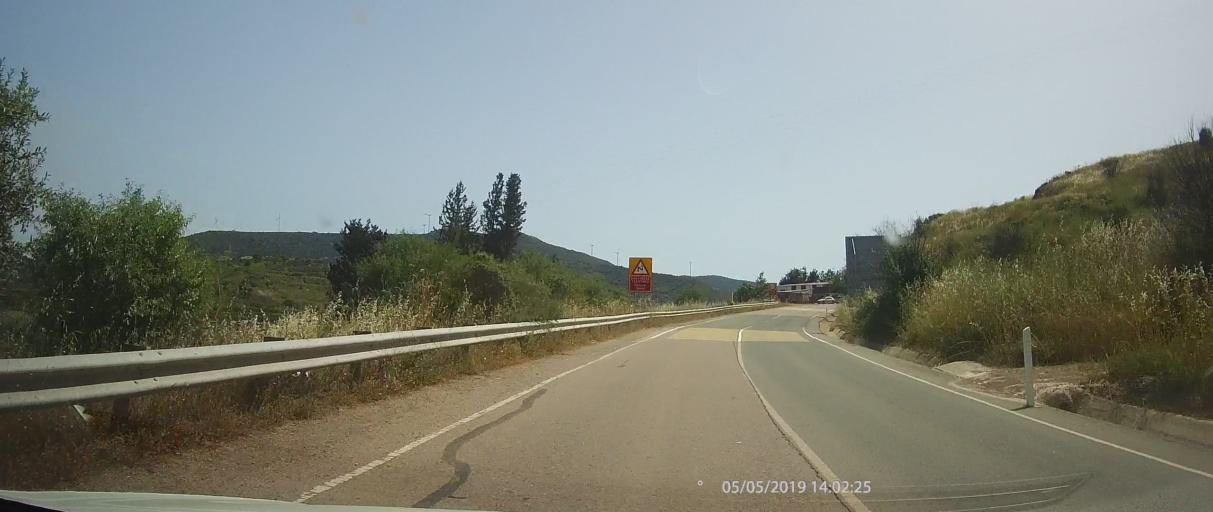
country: CY
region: Limassol
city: Pissouri
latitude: 34.7723
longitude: 32.6410
